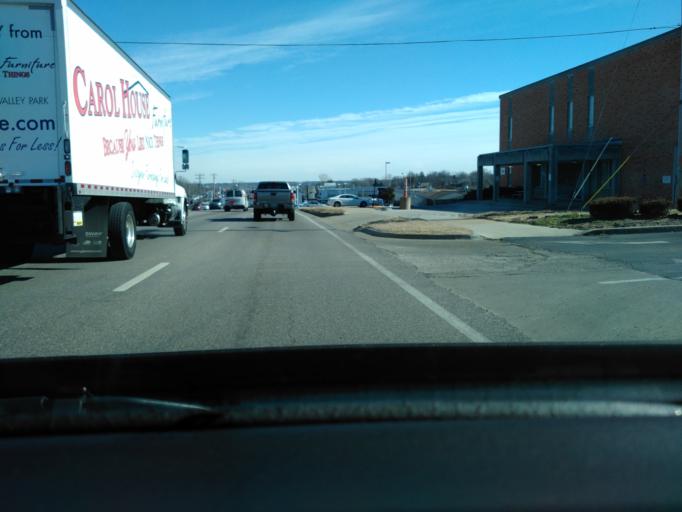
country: US
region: Missouri
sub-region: Saint Louis County
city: Winchester
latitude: 38.5929
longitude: -90.5368
